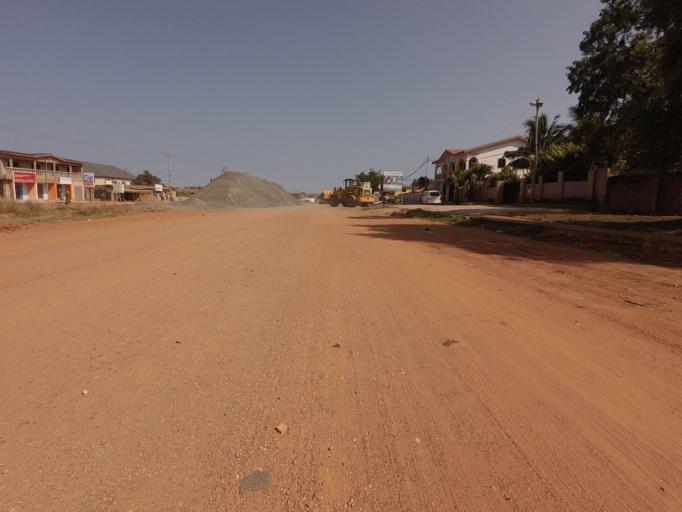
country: GH
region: Greater Accra
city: Teshi Old Town
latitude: 5.6095
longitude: -0.1233
